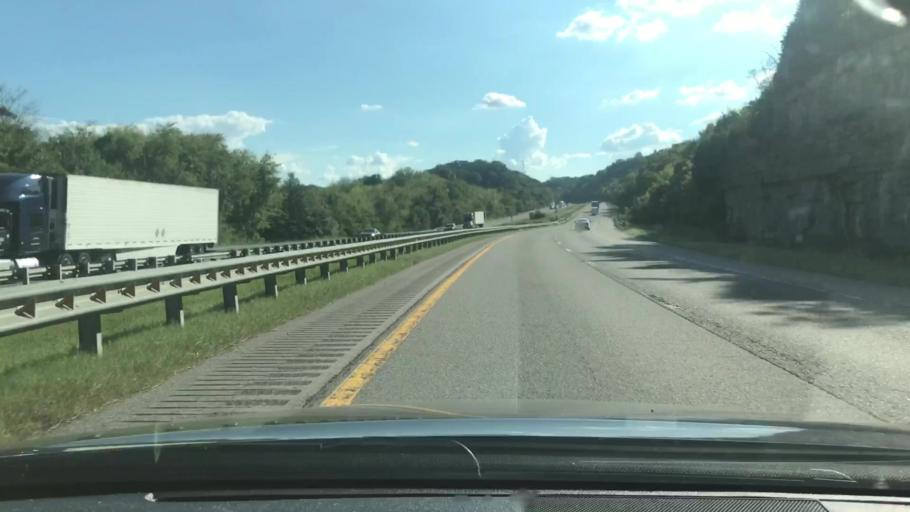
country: US
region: Tennessee
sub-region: Sumner County
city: Millersville
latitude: 36.3691
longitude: -86.7149
